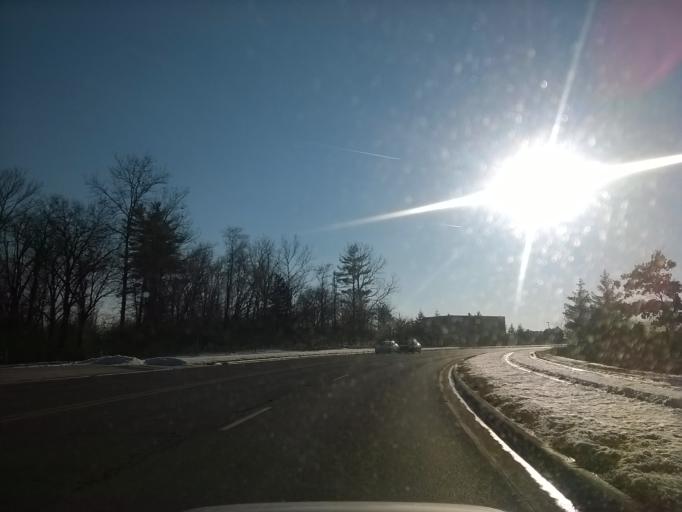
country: US
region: Indiana
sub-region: Hamilton County
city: Carmel
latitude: 39.9323
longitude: -86.0766
